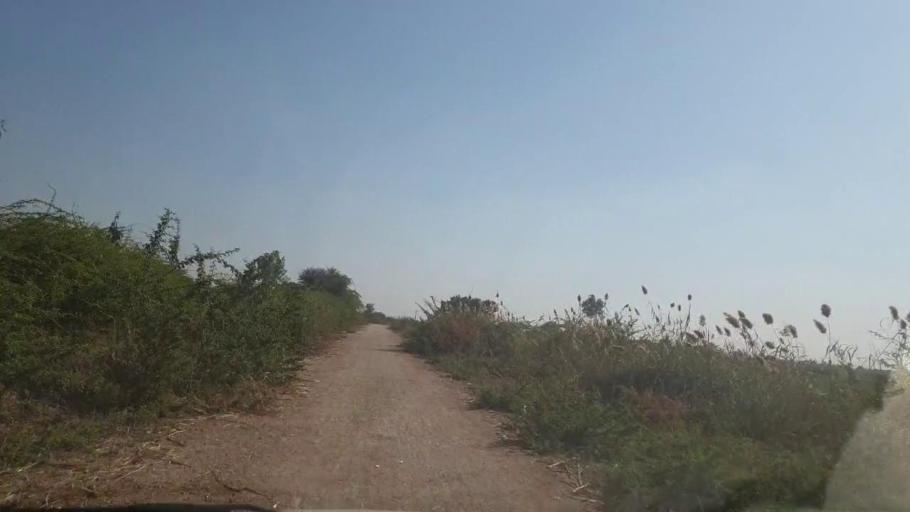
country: PK
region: Sindh
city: Mirpur Khas
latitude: 25.4578
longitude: 69.1259
